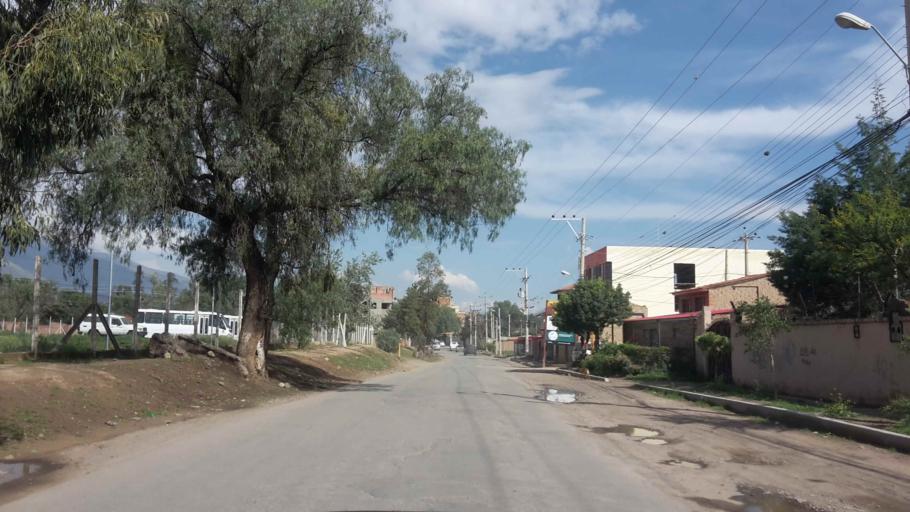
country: BO
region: Cochabamba
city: Cochabamba
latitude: -17.3365
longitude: -66.2285
